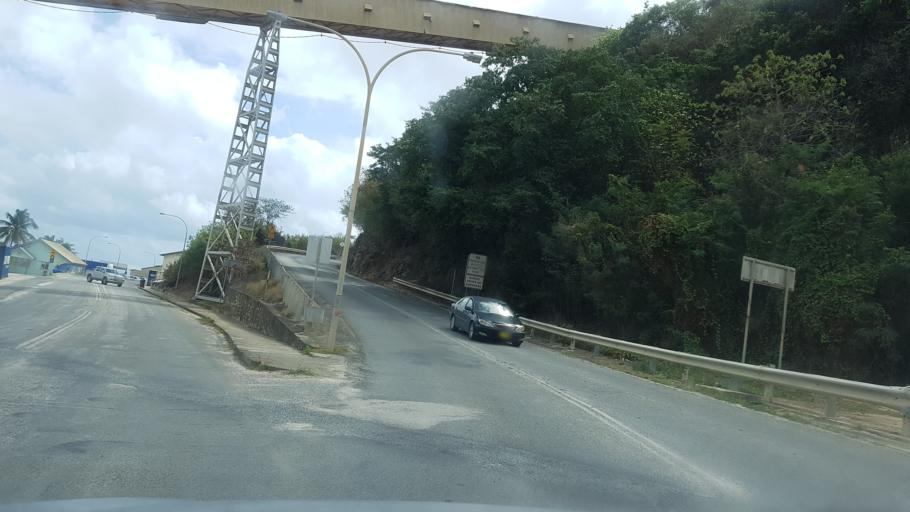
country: CX
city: Flying Fish Cove
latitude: -10.4186
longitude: 105.6744
